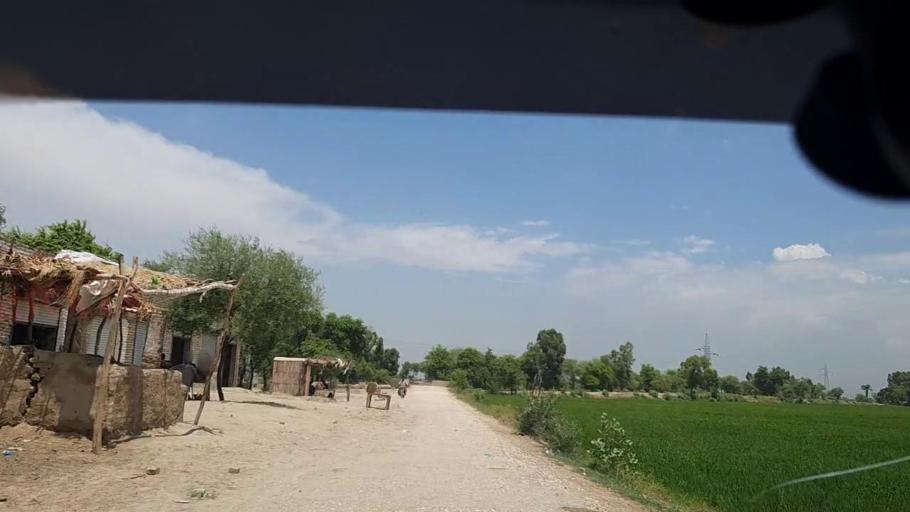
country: PK
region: Sindh
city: Ghauspur
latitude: 28.1026
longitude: 68.9860
